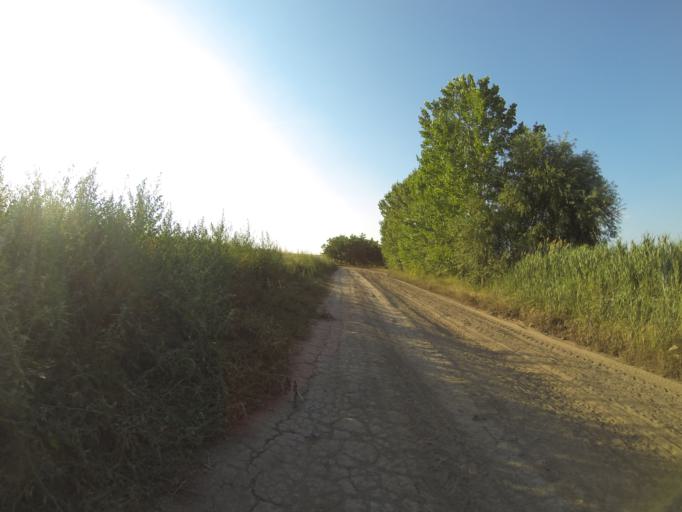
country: RO
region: Dolj
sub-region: Comuna Giurgita
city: Giurgita
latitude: 44.0155
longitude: 23.6724
